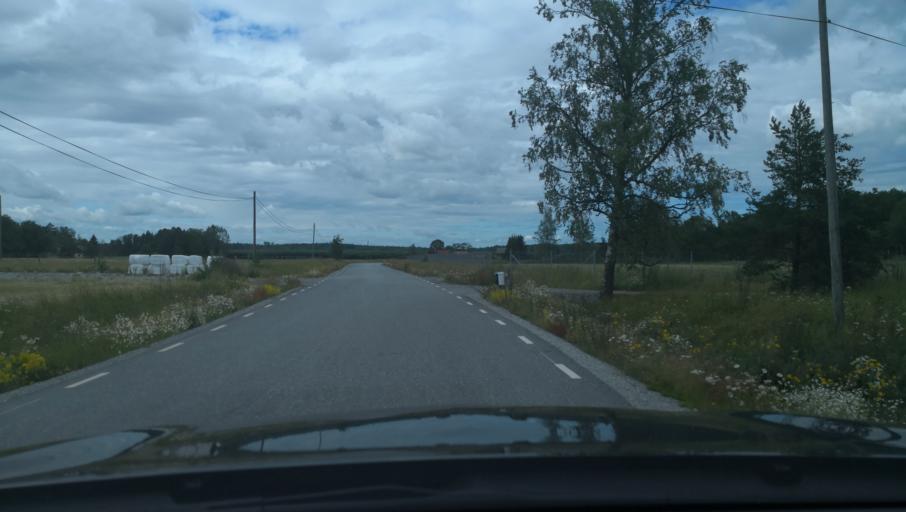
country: SE
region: Vaestmanland
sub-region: Hallstahammars Kommun
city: Hallstahammar
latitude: 59.6014
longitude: 16.1496
